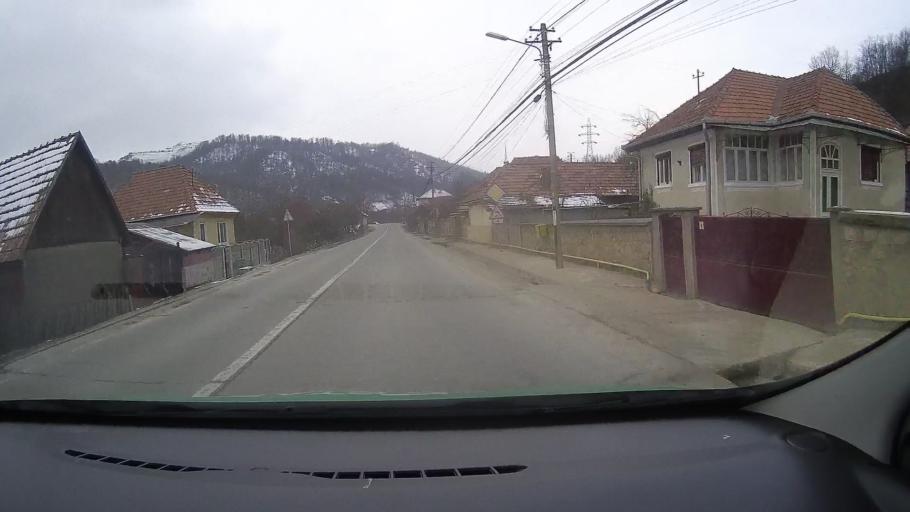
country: RO
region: Alba
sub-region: Oras Zlatna
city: Zlatna
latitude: 46.0909
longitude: 23.2622
